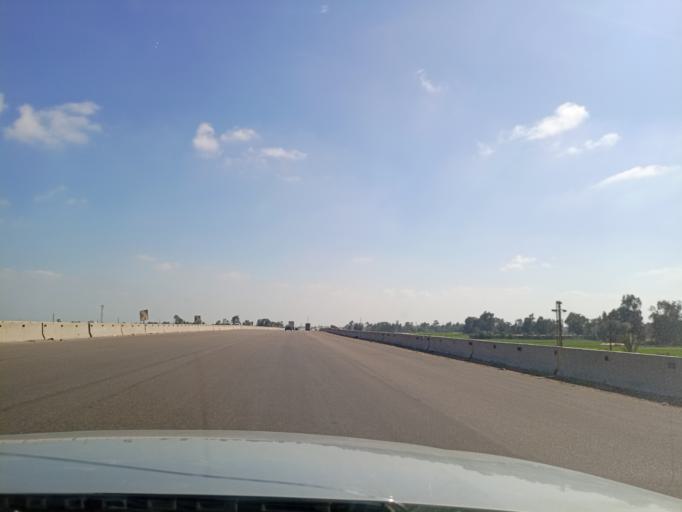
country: EG
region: Eastern Province
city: Mashtul as Suq
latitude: 30.4649
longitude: 31.3144
